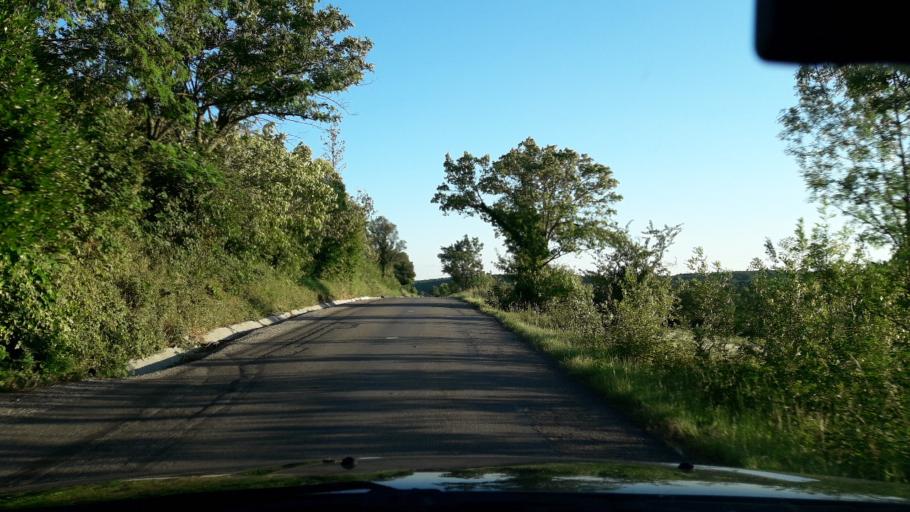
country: FR
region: Rhone-Alpes
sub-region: Departement de l'Ardeche
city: Lavilledieu
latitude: 44.6029
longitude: 4.4668
